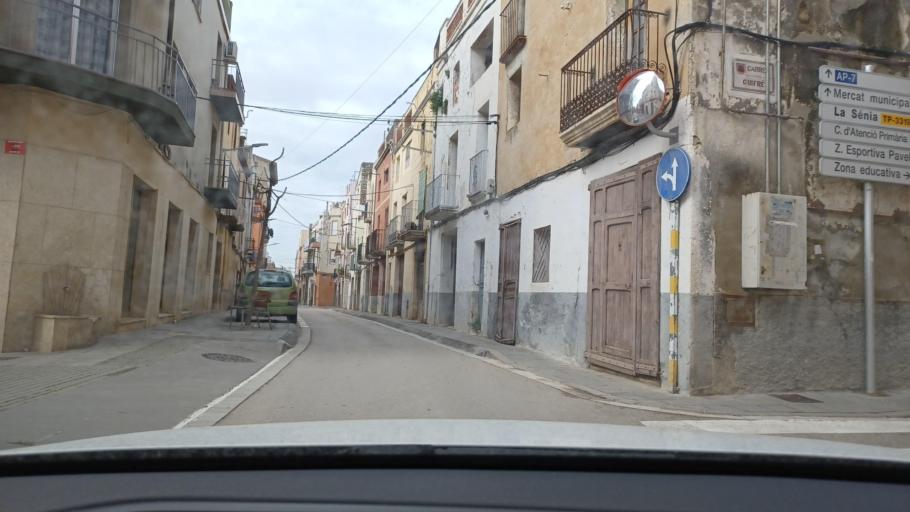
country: ES
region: Catalonia
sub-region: Provincia de Tarragona
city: Ulldecona
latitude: 40.5982
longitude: 0.4462
